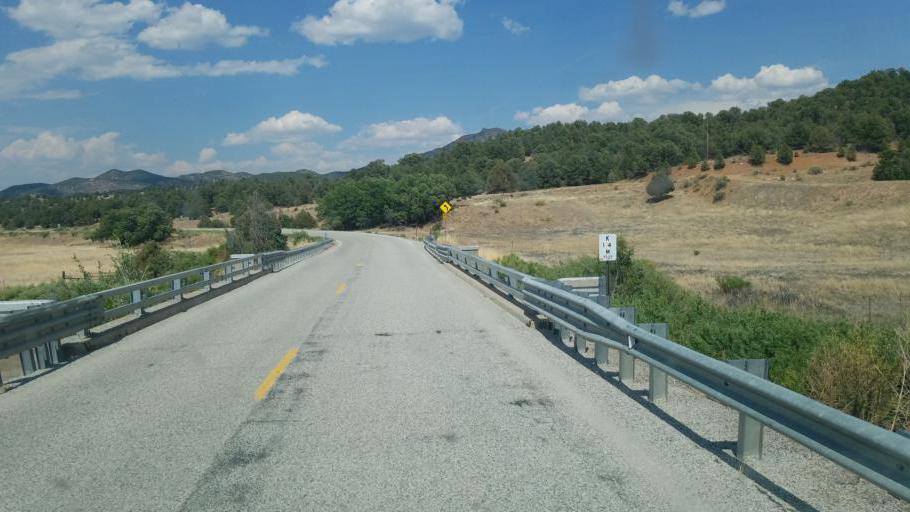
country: US
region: Colorado
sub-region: Custer County
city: Westcliffe
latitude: 38.3345
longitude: -105.5987
